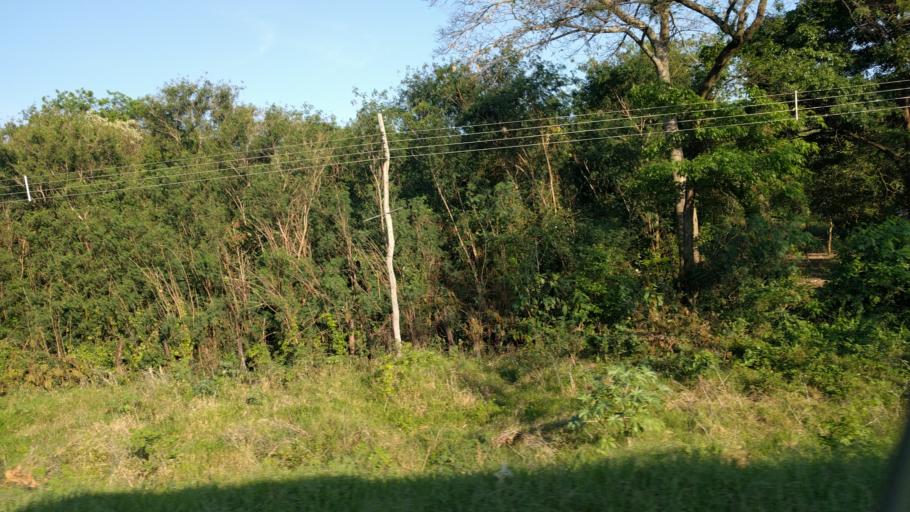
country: BO
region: Santa Cruz
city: Jorochito
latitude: -18.0616
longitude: -63.4328
